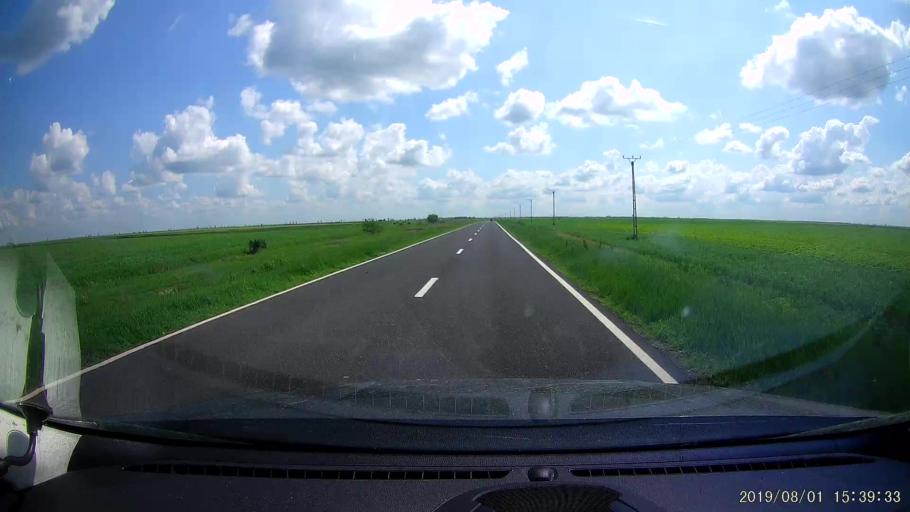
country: RO
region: Braila
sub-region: Comuna Baraganul
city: Baraganul
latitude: 44.8548
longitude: 27.5573
